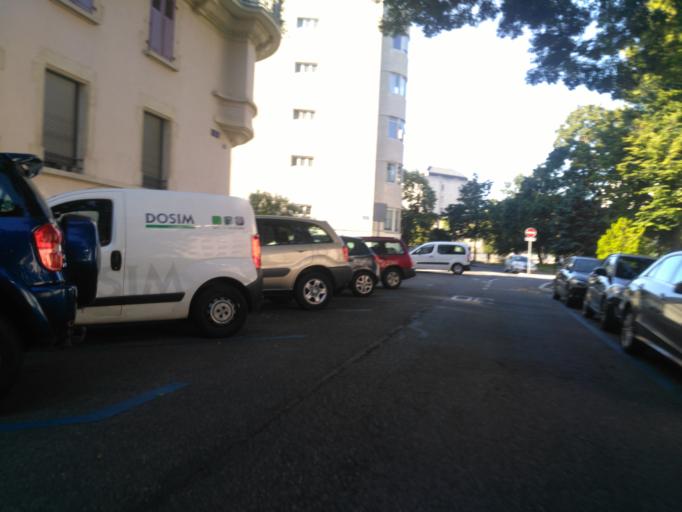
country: CH
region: Geneva
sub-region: Geneva
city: Geneve
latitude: 46.2065
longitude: 6.1286
